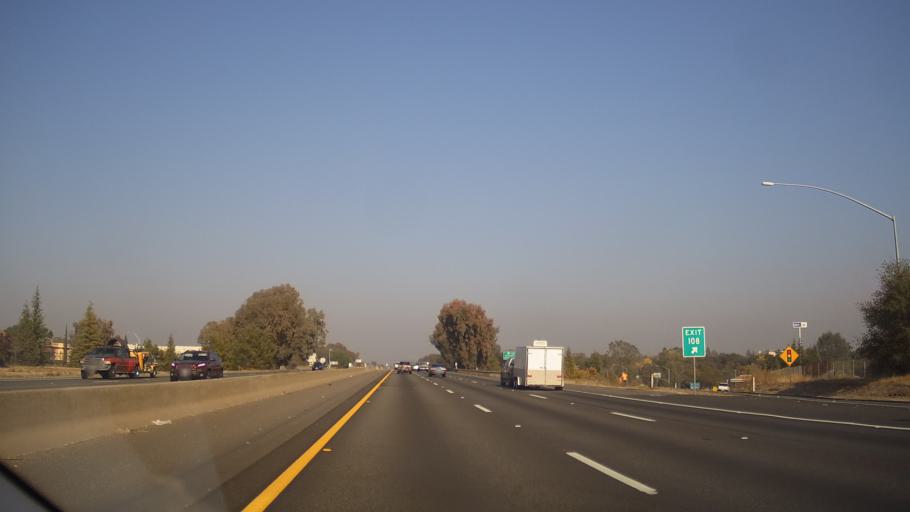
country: US
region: California
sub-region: Placer County
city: Rocklin
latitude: 38.7872
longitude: -121.2241
